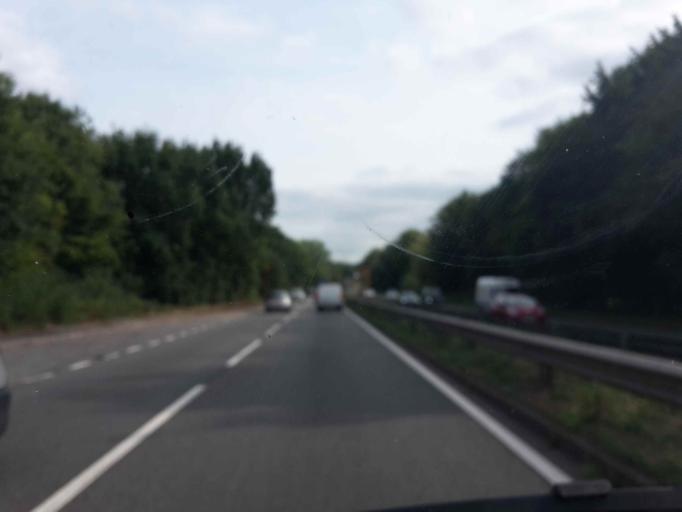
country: GB
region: England
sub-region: Surrey
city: Bagshot
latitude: 51.3632
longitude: -0.6852
